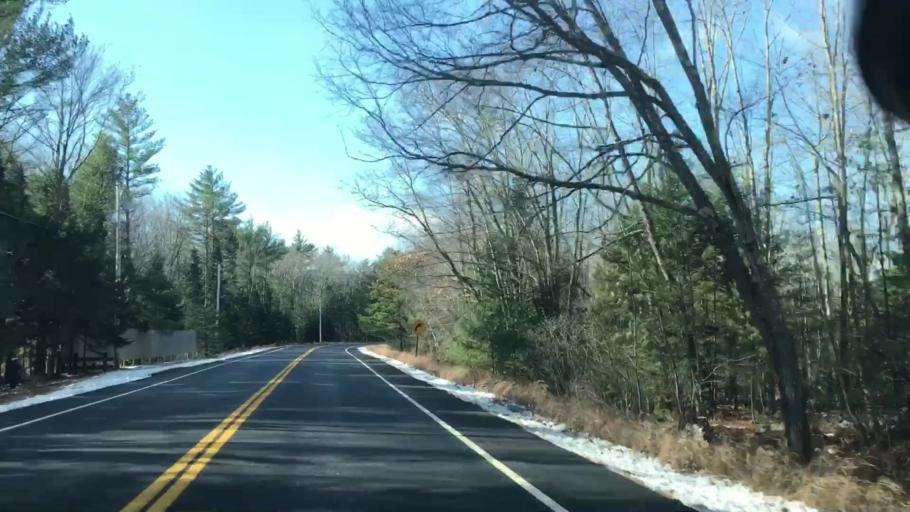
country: US
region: Maine
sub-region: Oxford County
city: Porter
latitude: 43.7884
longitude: -70.9659
